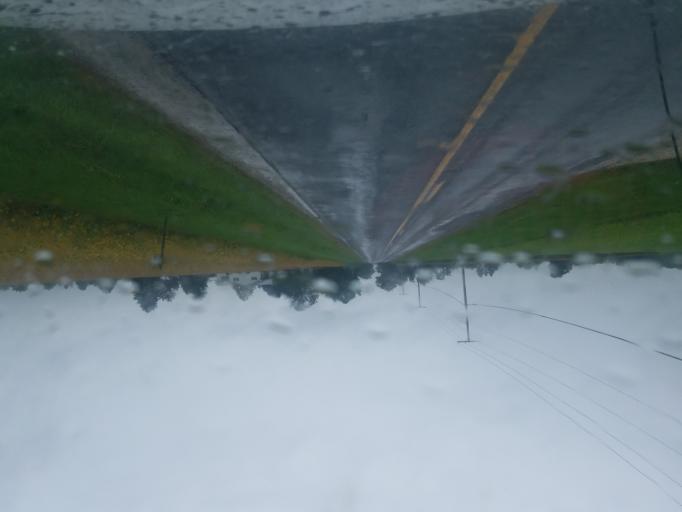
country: US
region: Ohio
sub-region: Medina County
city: Seville
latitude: 41.0180
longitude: -81.8326
